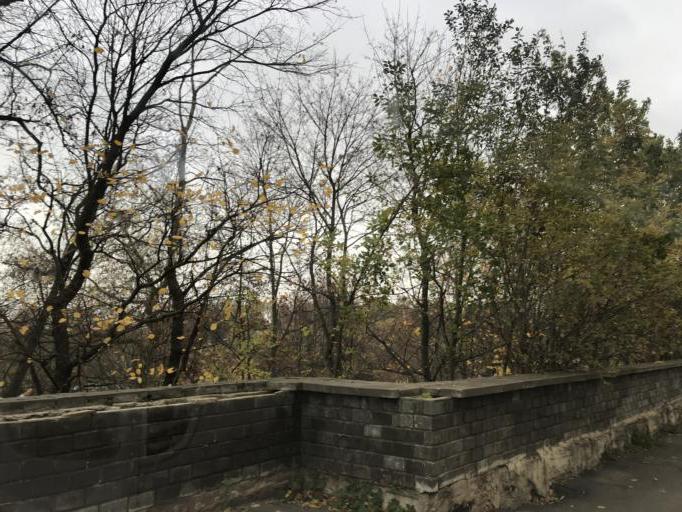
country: BY
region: Mogilev
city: Mahilyow
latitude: 53.9003
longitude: 30.3479
